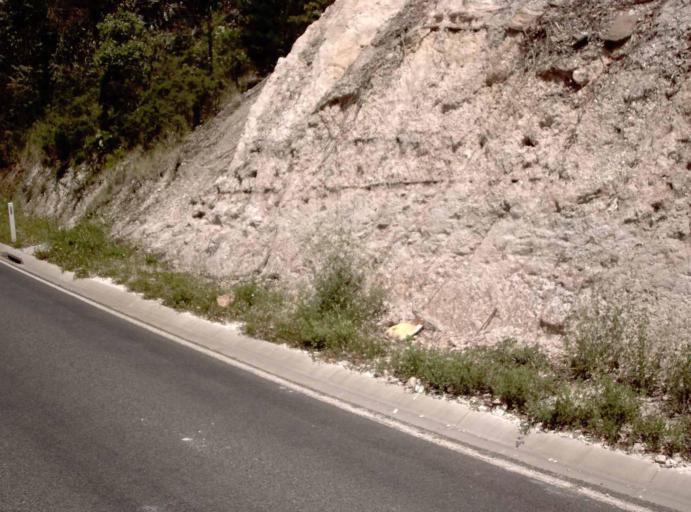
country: AU
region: Victoria
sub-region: Latrobe
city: Traralgon
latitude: -38.3628
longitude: 146.7589
